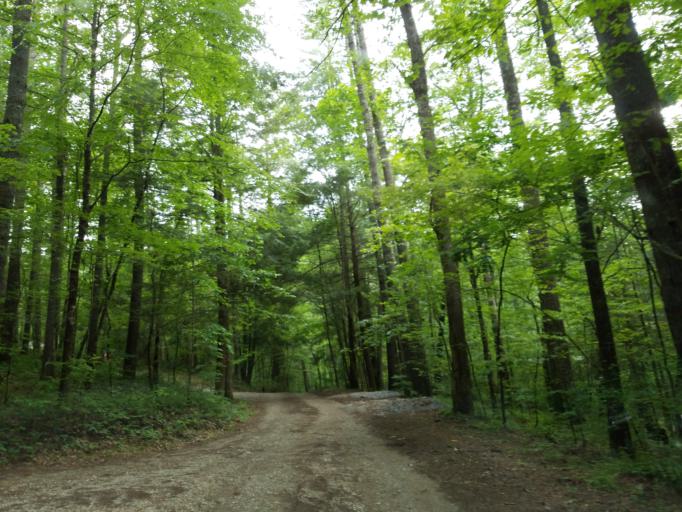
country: US
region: Georgia
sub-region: Union County
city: Blairsville
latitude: 34.7633
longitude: -84.0672
